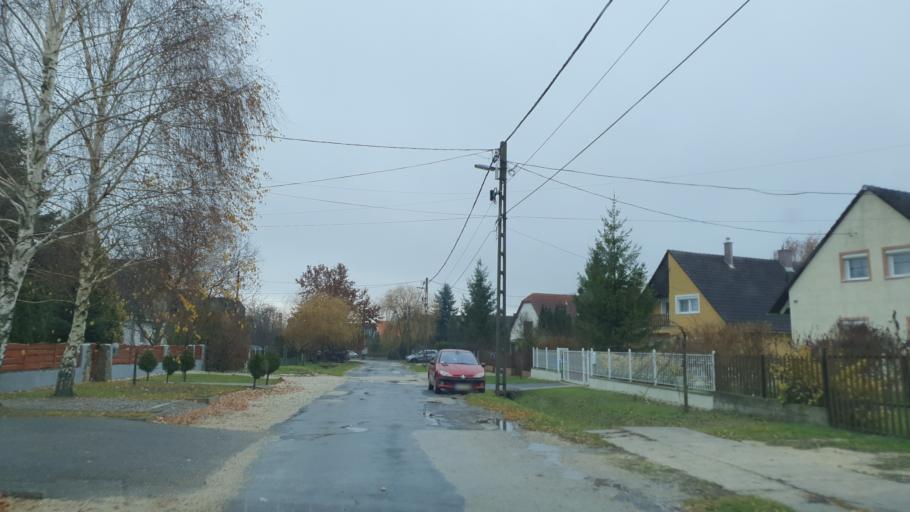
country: HU
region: Veszprem
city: Veszprem
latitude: 47.1378
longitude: 17.9426
